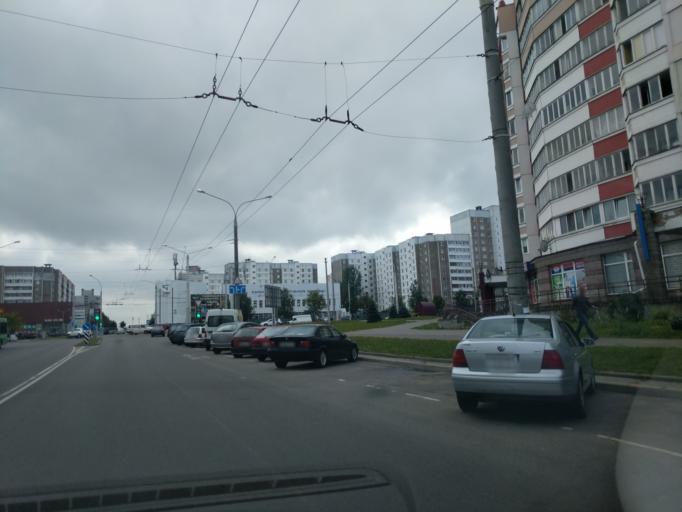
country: BY
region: Minsk
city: Novoye Medvezhino
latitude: 53.8886
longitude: 27.4219
